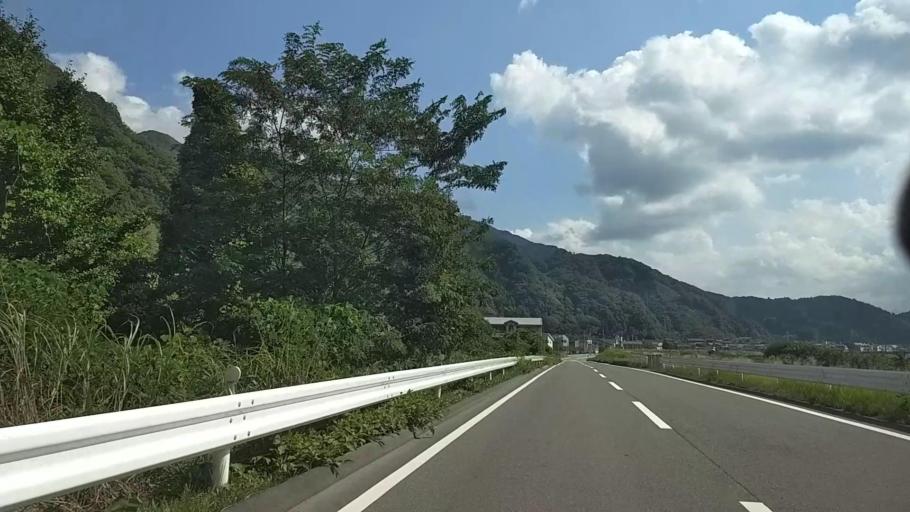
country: JP
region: Shizuoka
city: Fujinomiya
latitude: 35.3721
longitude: 138.4531
